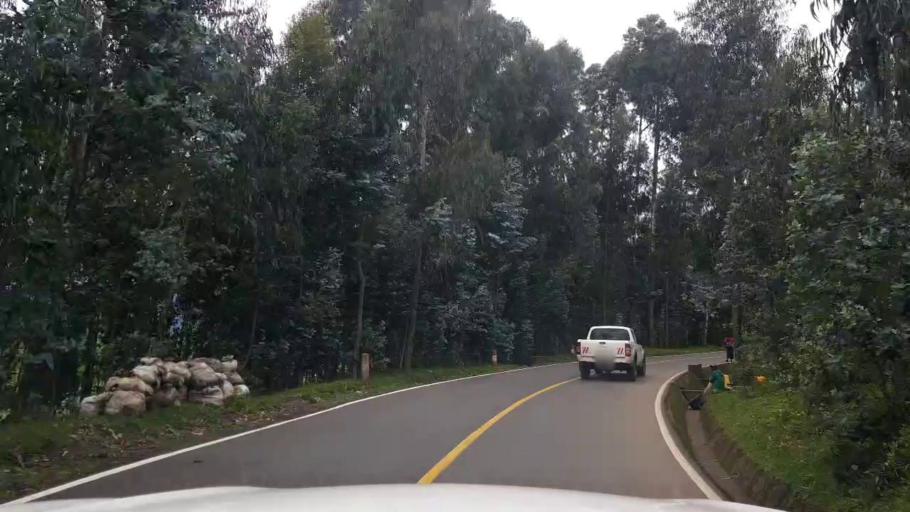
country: RW
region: Northern Province
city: Musanze
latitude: -1.4372
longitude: 29.5524
